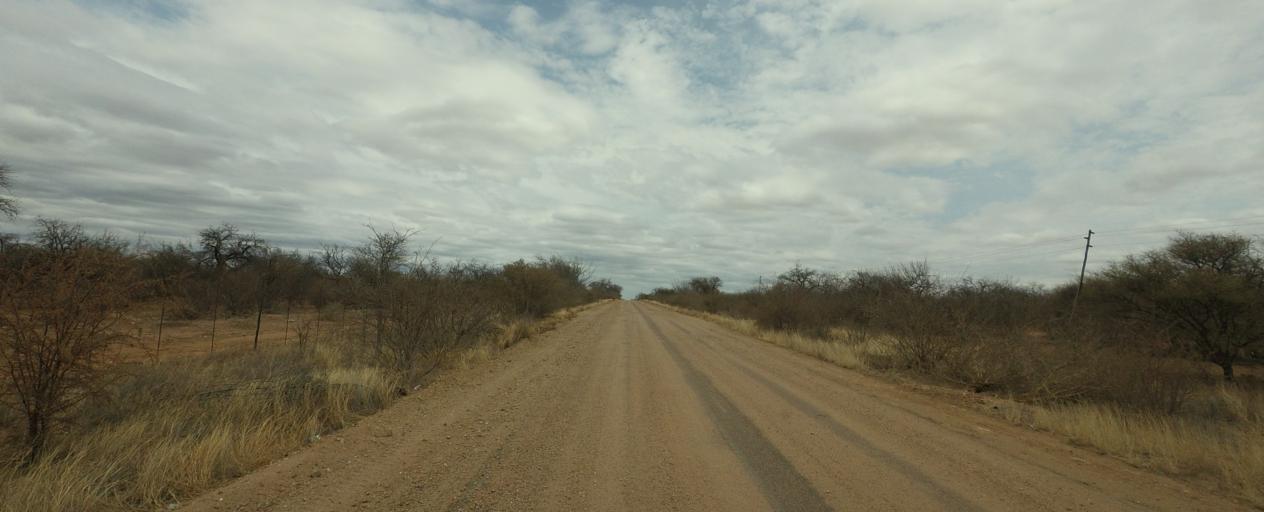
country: BW
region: Central
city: Mathathane
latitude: -22.6711
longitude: 28.6825
